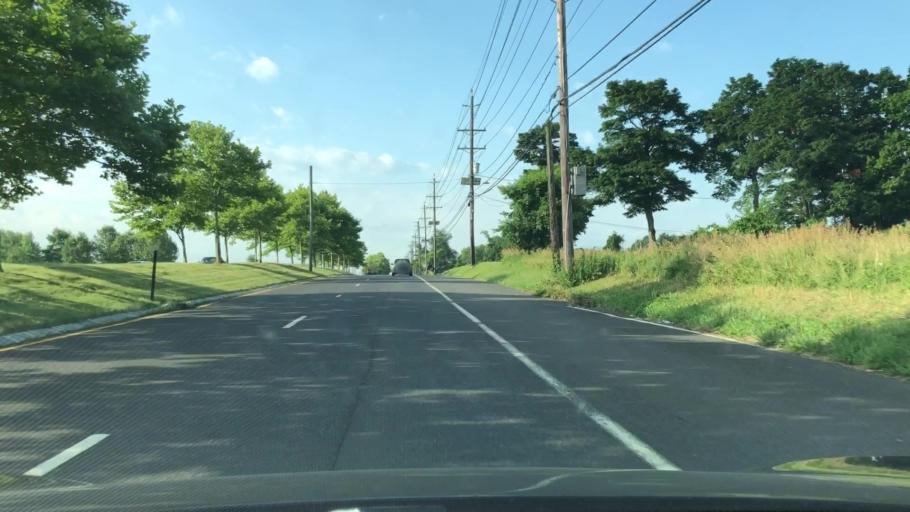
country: US
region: New Jersey
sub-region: Mercer County
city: Ewing
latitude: 40.3008
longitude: -74.8117
